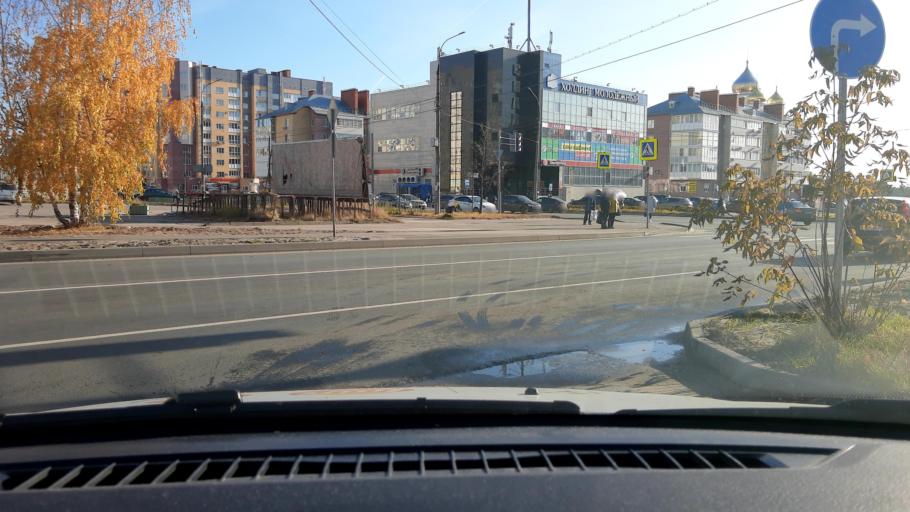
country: RU
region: Nizjnij Novgorod
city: Dzerzhinsk
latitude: 56.2312
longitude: 43.4103
